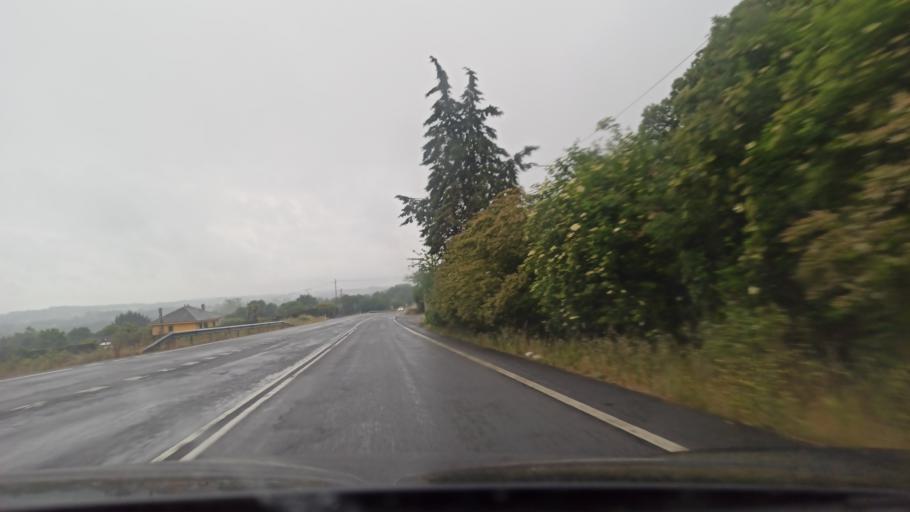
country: ES
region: Galicia
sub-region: Provincia de Lugo
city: Guntin
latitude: 42.9244
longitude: -7.6438
